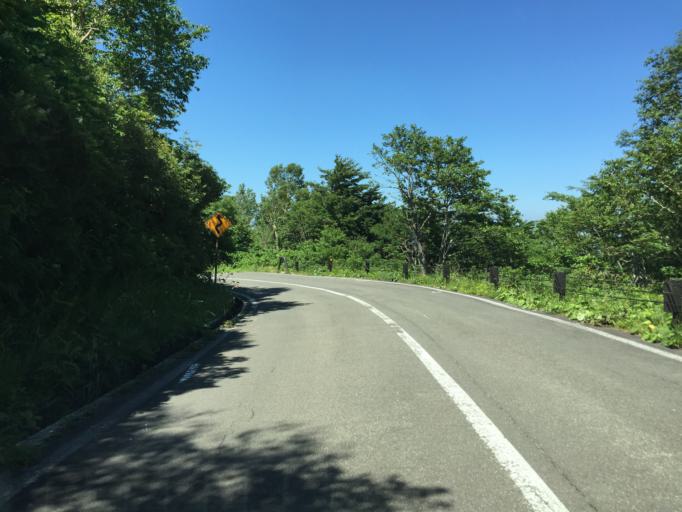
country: JP
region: Fukushima
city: Fukushima-shi
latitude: 37.7466
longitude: 140.2812
